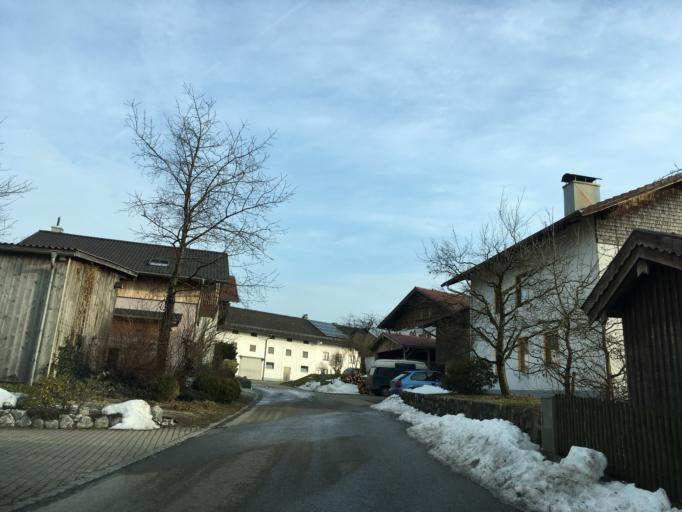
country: DE
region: Bavaria
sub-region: Upper Bavaria
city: Sochtenau
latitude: 47.9402
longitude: 12.2312
